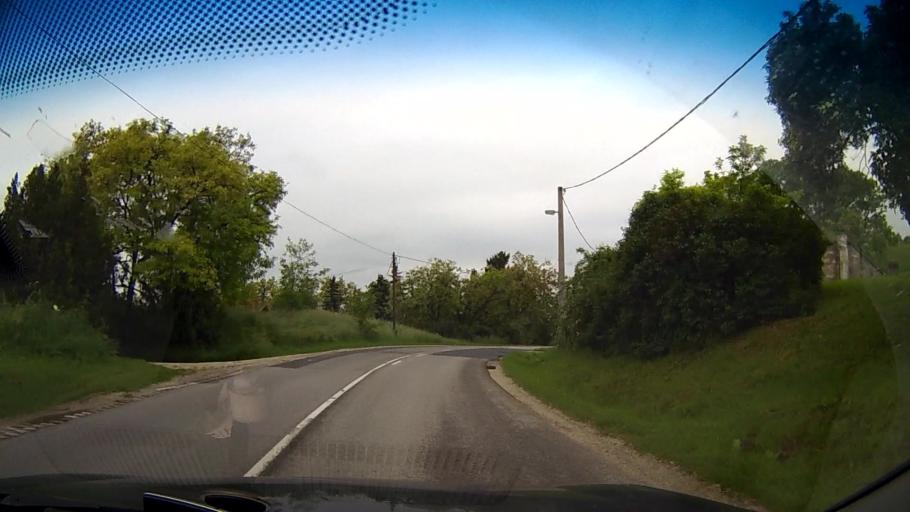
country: HU
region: Pest
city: Perbal
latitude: 47.5728
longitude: 18.7370
